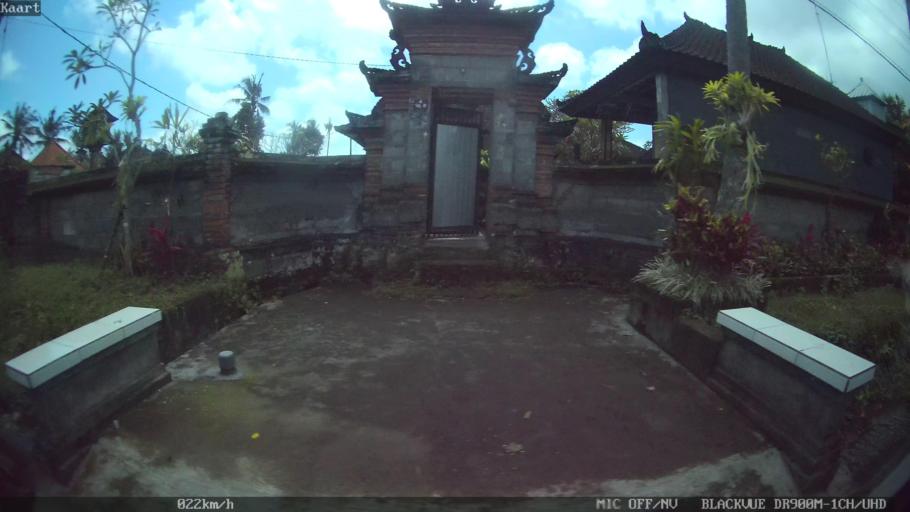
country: ID
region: Bali
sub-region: Kabupaten Gianyar
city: Ubud
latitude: -8.5401
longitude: 115.2807
